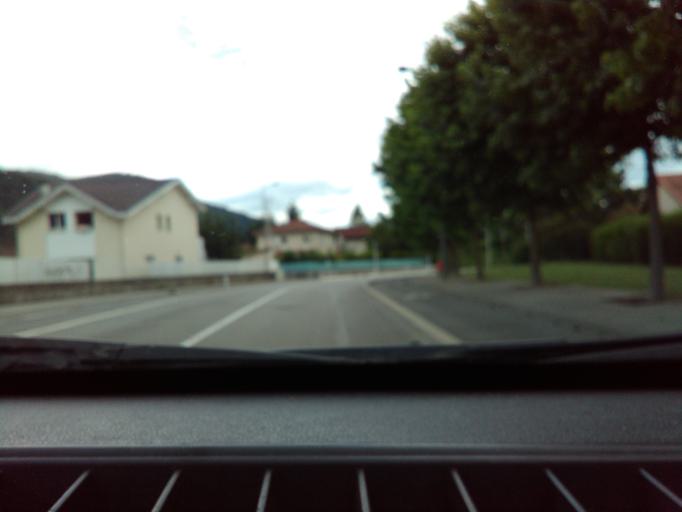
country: FR
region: Rhone-Alpes
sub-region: Departement de l'Isere
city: Saint-Martin-d'Heres
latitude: 45.1817
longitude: 5.7681
